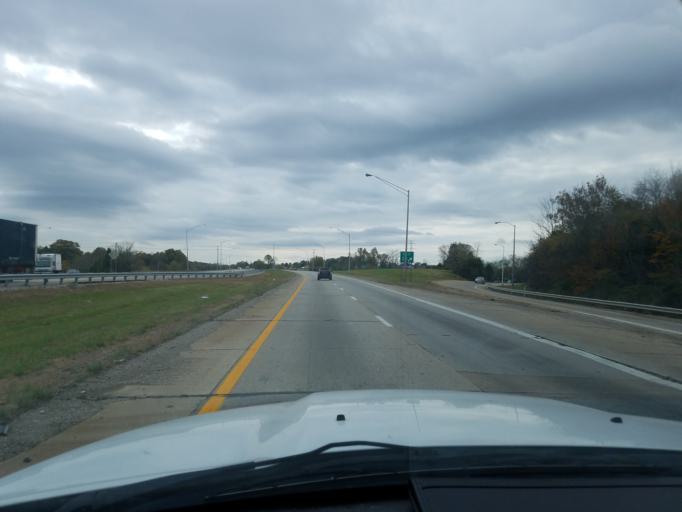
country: US
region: Kentucky
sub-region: Jefferson County
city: Jeffersontown
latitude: 38.1921
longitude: -85.5090
